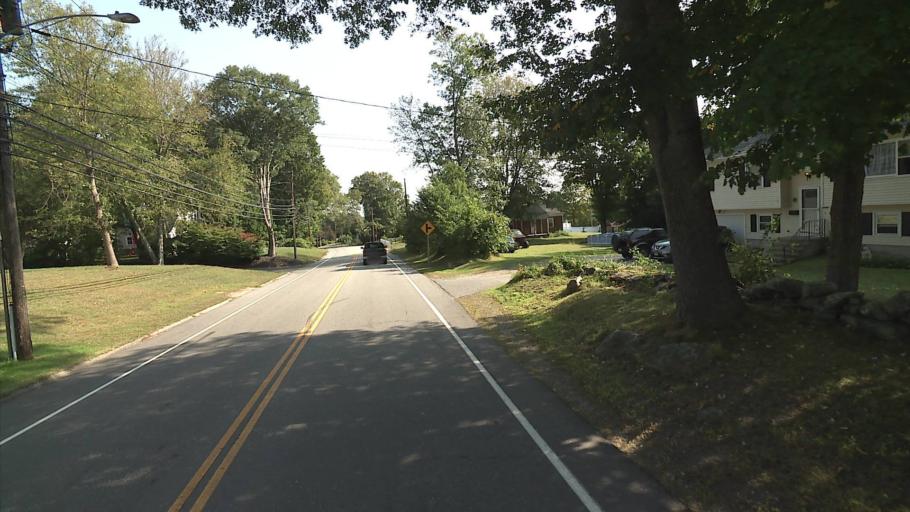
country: US
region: Connecticut
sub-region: New London County
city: Norwich
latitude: 41.5609
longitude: -72.0684
